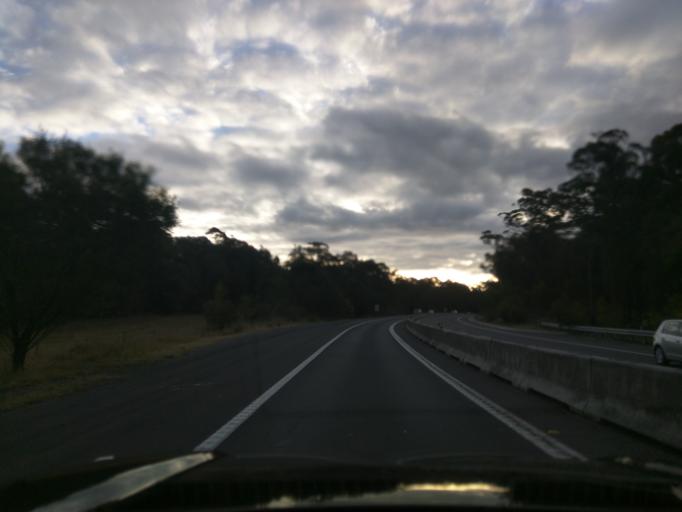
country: AU
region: New South Wales
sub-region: Wollondilly
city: Douglas Park
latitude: -34.2854
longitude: 150.7184
